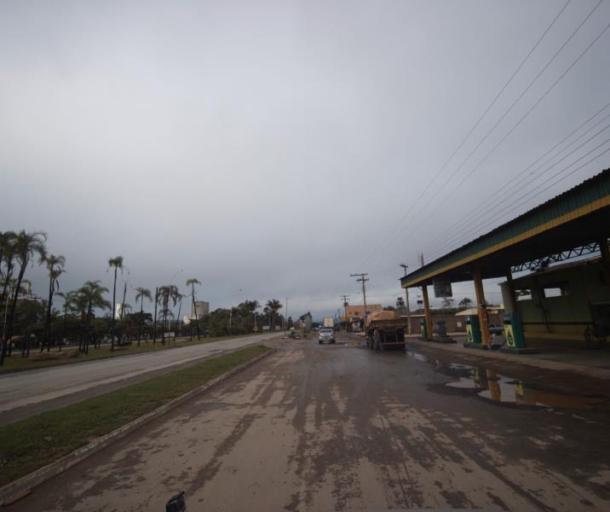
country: BR
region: Goias
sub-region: Pirenopolis
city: Pirenopolis
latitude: -15.7859
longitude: -48.7704
